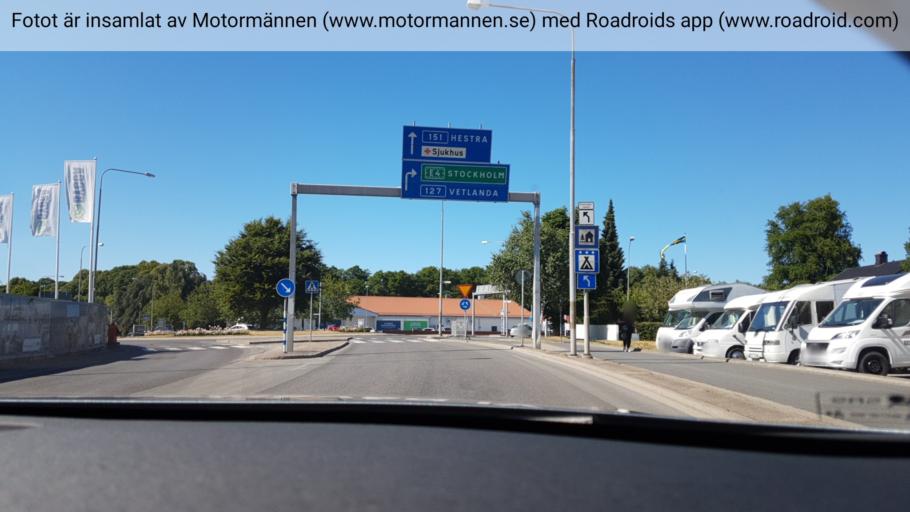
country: SE
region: Joenkoeping
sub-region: Varnamo Kommun
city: Varnamo
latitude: 57.1836
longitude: 14.0579
